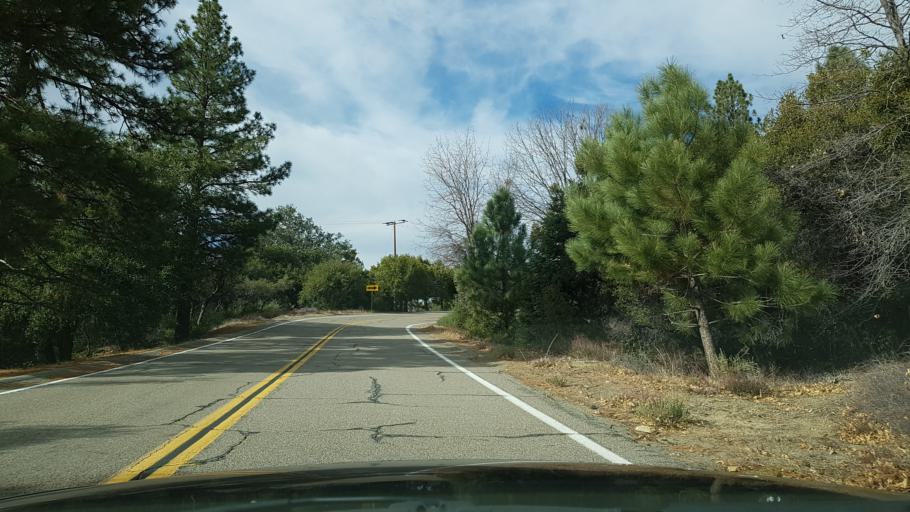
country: US
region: California
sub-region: Riverside County
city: Aguanga
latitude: 33.3583
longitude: -116.8716
